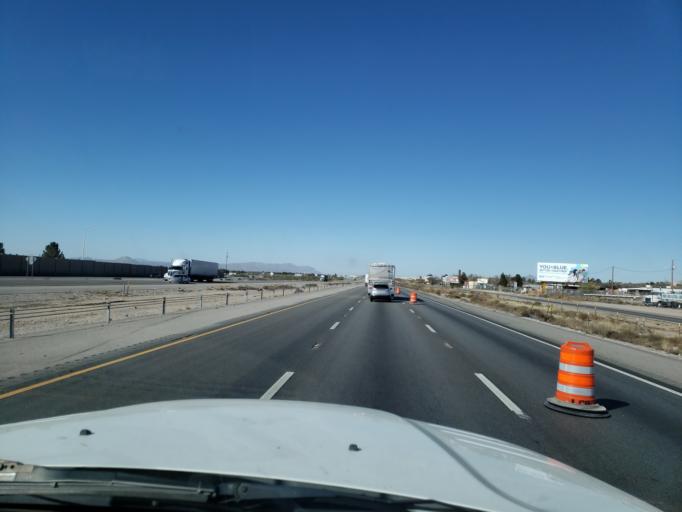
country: US
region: New Mexico
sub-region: Dona Ana County
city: University Park
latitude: 32.2482
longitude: -106.7230
